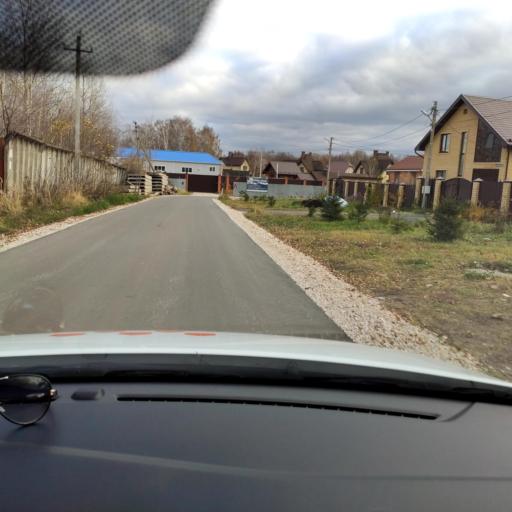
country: RU
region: Tatarstan
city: Stolbishchi
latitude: 55.7368
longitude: 49.2673
